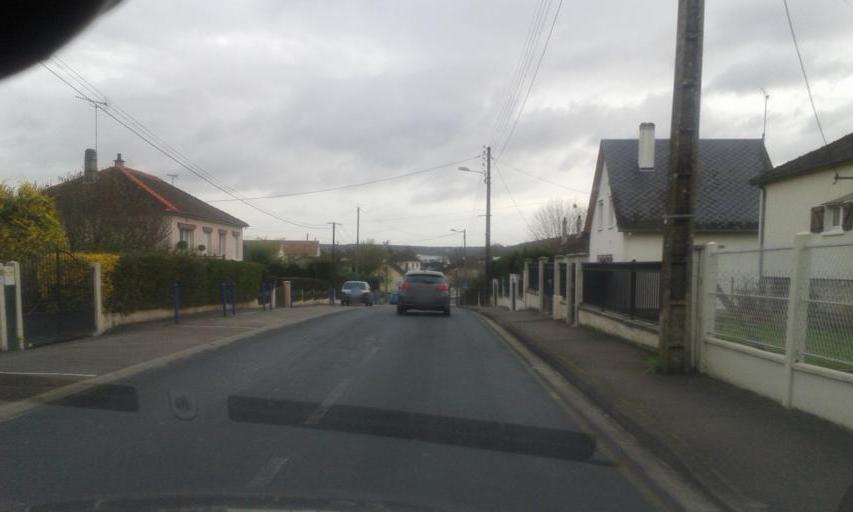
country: FR
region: Haute-Normandie
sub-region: Departement de l'Eure
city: Fleury-sur-Andelle
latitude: 49.3639
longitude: 1.3541
